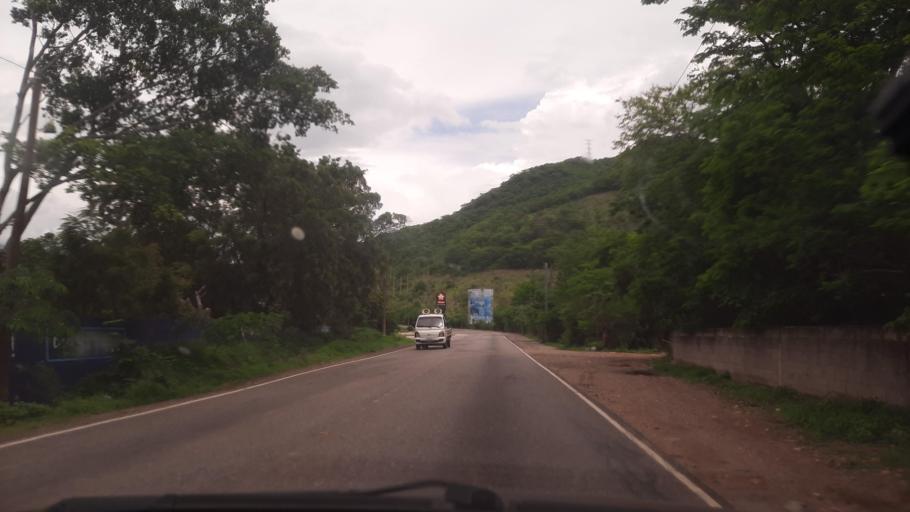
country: GT
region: Zacapa
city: San Jorge
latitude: 14.8954
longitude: -89.5218
